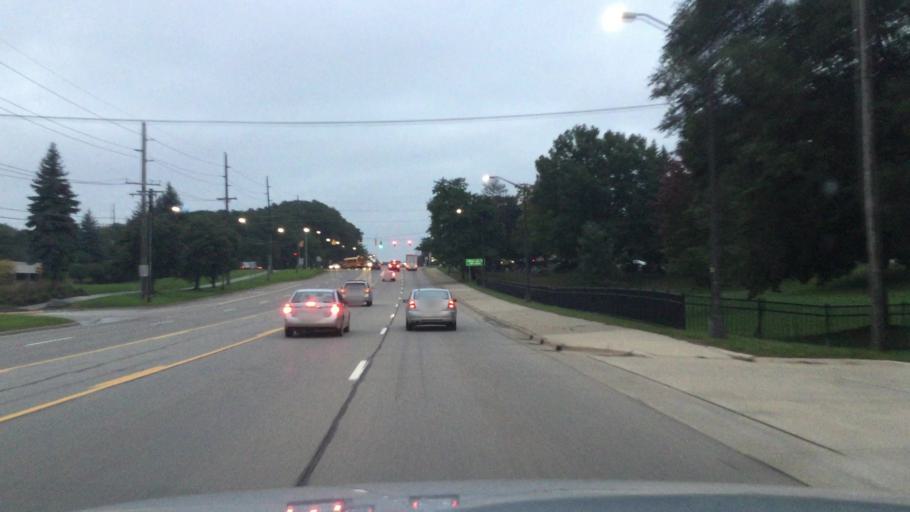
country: US
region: Michigan
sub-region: Oakland County
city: Clarkston
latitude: 42.7245
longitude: -83.4271
